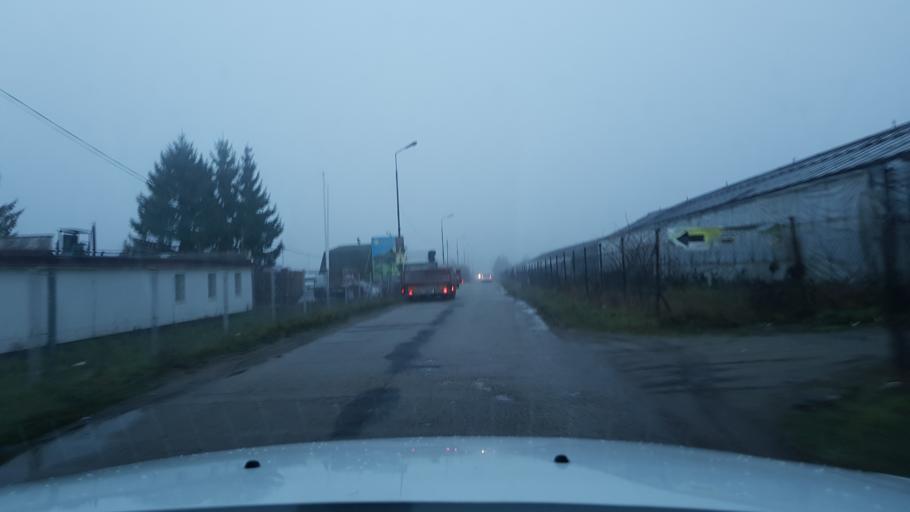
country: PL
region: West Pomeranian Voivodeship
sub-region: Powiat policki
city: Przeclaw
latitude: 53.3898
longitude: 14.4866
